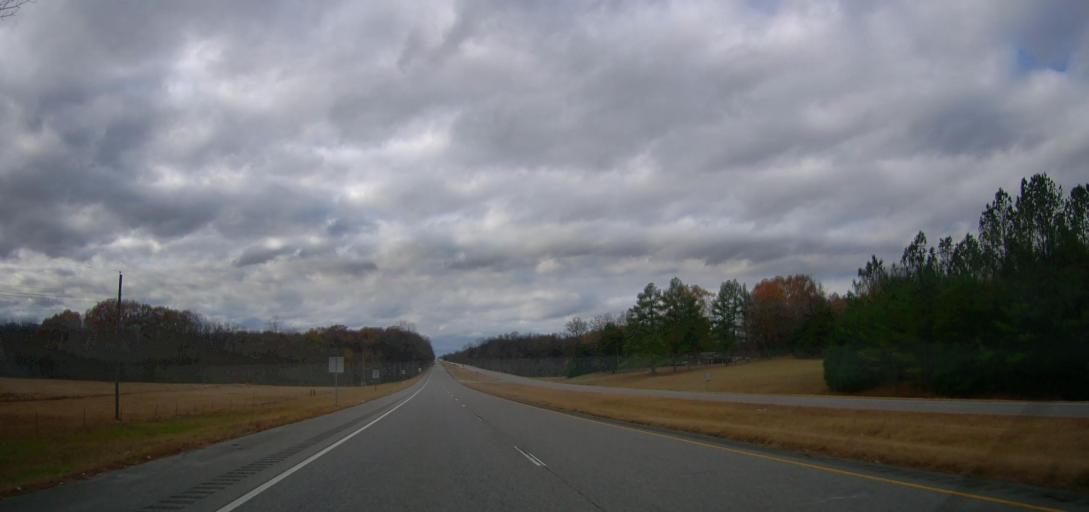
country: US
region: Alabama
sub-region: Lawrence County
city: Town Creek
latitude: 34.6283
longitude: -87.4801
